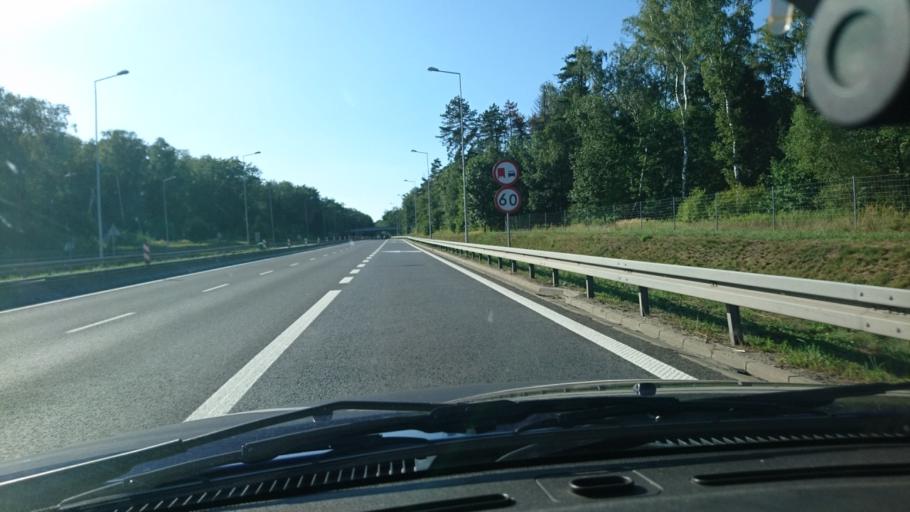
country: PL
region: Silesian Voivodeship
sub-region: Gliwice
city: Gliwice
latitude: 50.3090
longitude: 18.7184
